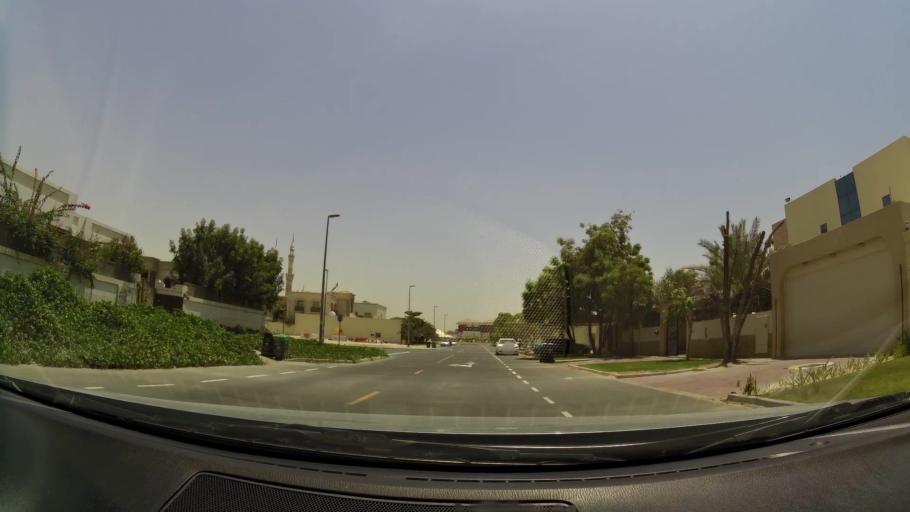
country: AE
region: Dubai
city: Dubai
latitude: 25.0947
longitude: 55.1990
